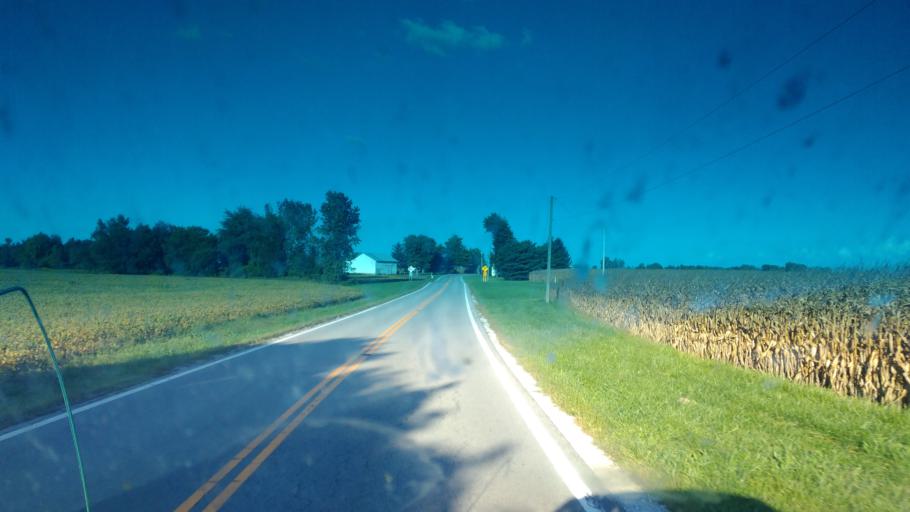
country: US
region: Ohio
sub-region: Wyandot County
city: Carey
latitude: 40.9366
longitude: -83.4127
